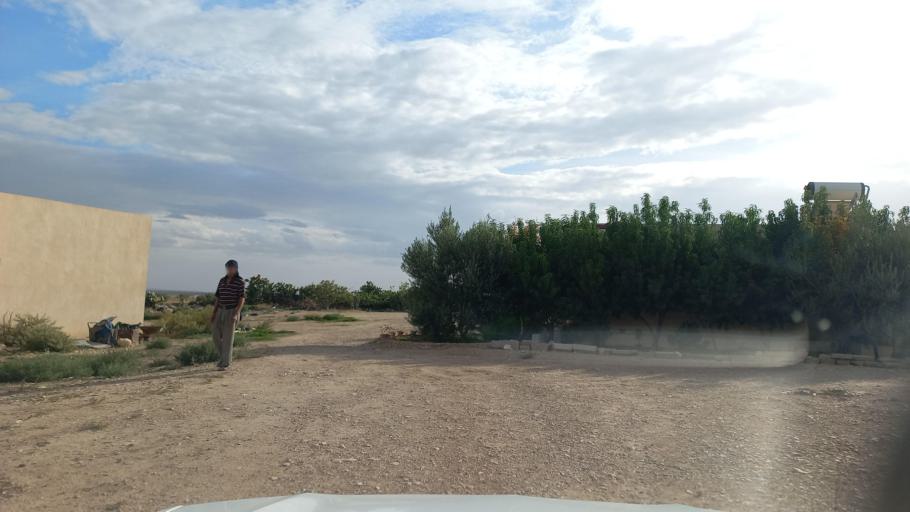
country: TN
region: Al Qasrayn
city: Sbiba
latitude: 35.4440
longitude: 9.0750
